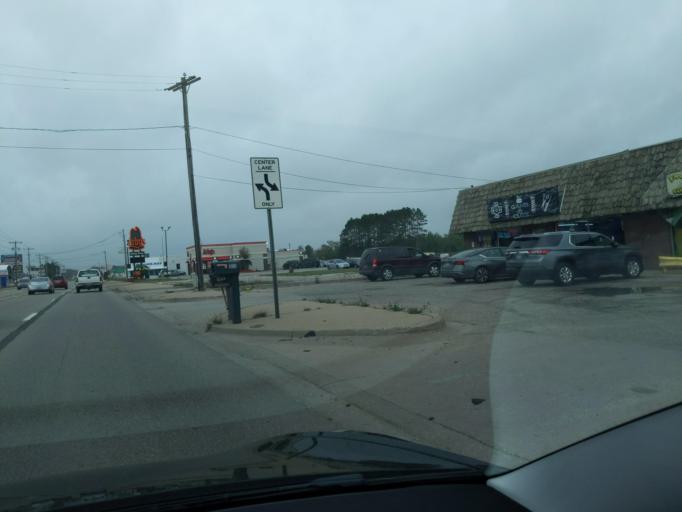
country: US
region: Michigan
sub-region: Wexford County
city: Cadillac
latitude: 44.2748
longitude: -85.4065
